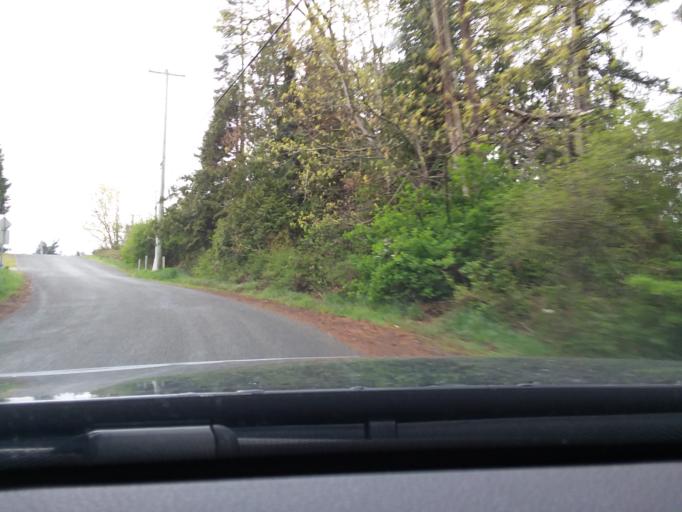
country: CA
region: British Columbia
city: North Saanich
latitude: 48.5542
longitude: -123.3908
